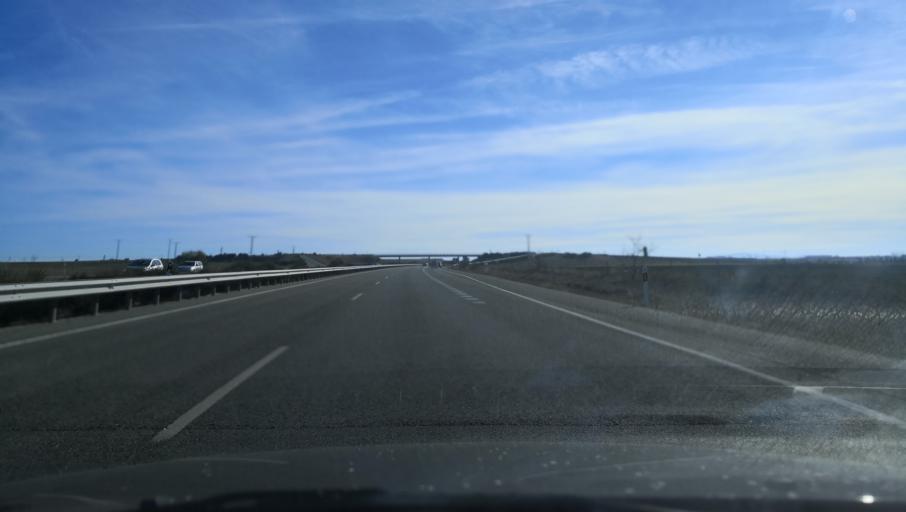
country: ES
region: Castille and Leon
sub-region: Provincia de Salamanca
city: Penaranda de Bracamonte
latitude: 40.9171
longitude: -5.1970
